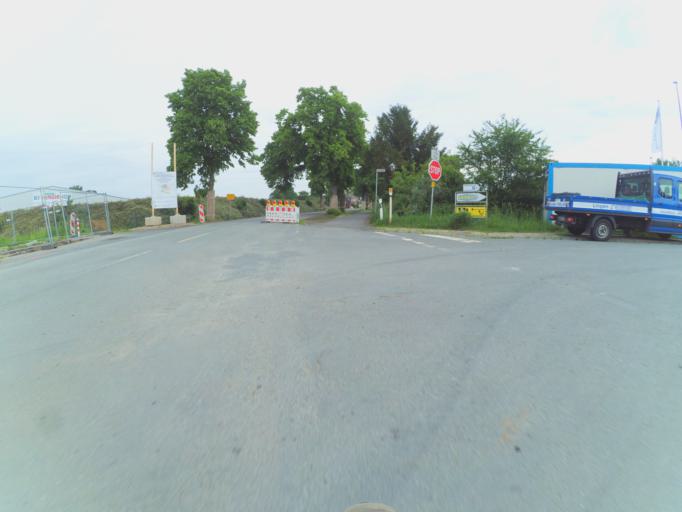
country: DE
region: North Rhine-Westphalia
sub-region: Regierungsbezirk Munster
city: Birgte
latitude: 52.2999
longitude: 7.6569
